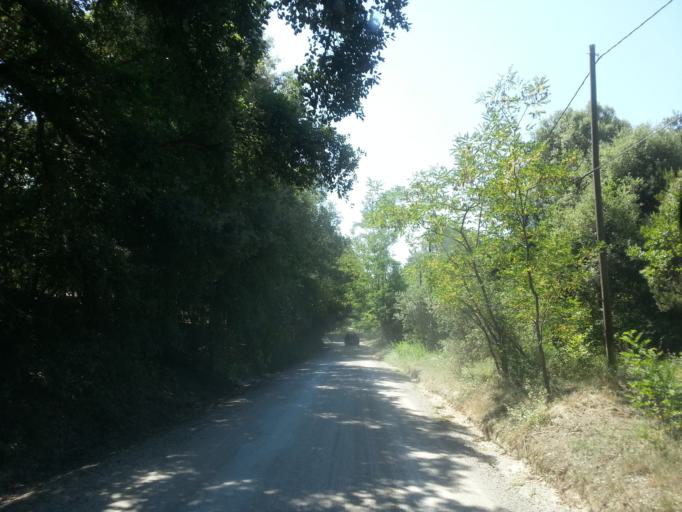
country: ES
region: Catalonia
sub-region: Provincia de Barcelona
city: Campins
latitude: 41.7378
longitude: 2.5001
